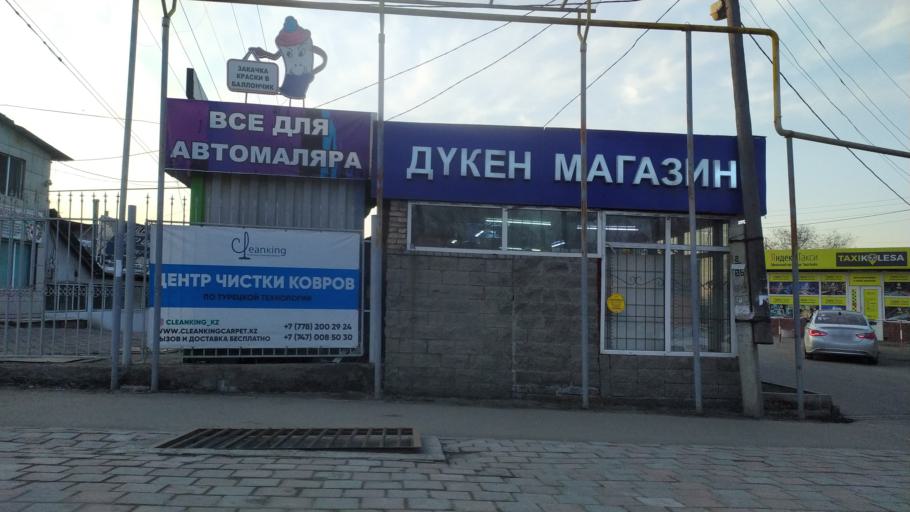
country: KZ
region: Almaty Qalasy
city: Almaty
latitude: 43.2224
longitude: 76.8841
